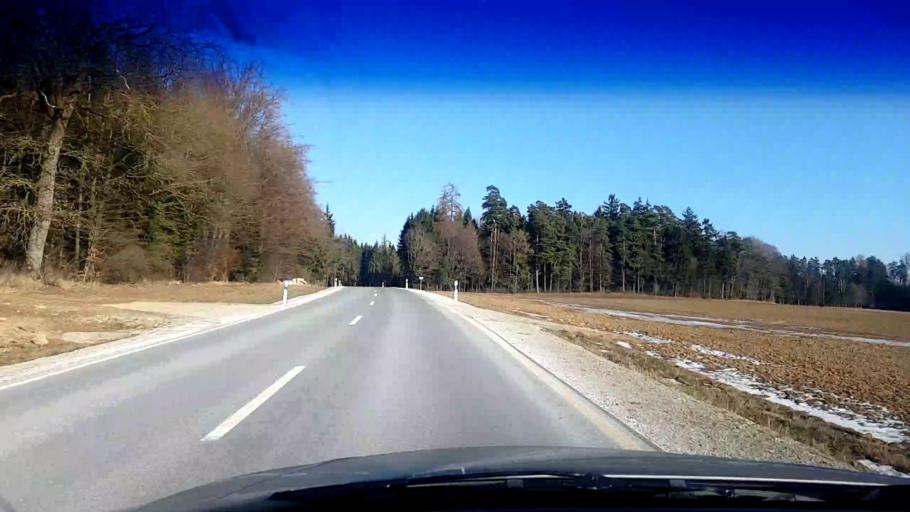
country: DE
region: Bavaria
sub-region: Upper Franconia
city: Heiligenstadt
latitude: 49.8780
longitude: 11.1957
